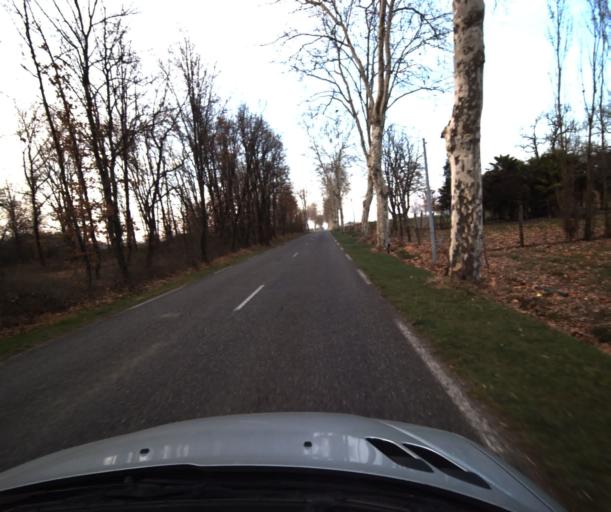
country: FR
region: Midi-Pyrenees
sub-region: Departement du Tarn-et-Garonne
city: Labastide-Saint-Pierre
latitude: 43.8791
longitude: 1.3775
